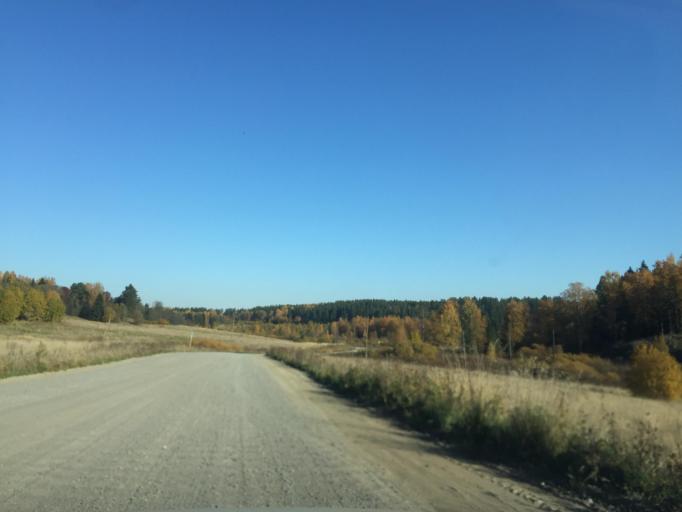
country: RU
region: Leningrad
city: Kuznechnoye
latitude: 61.3082
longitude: 29.9311
